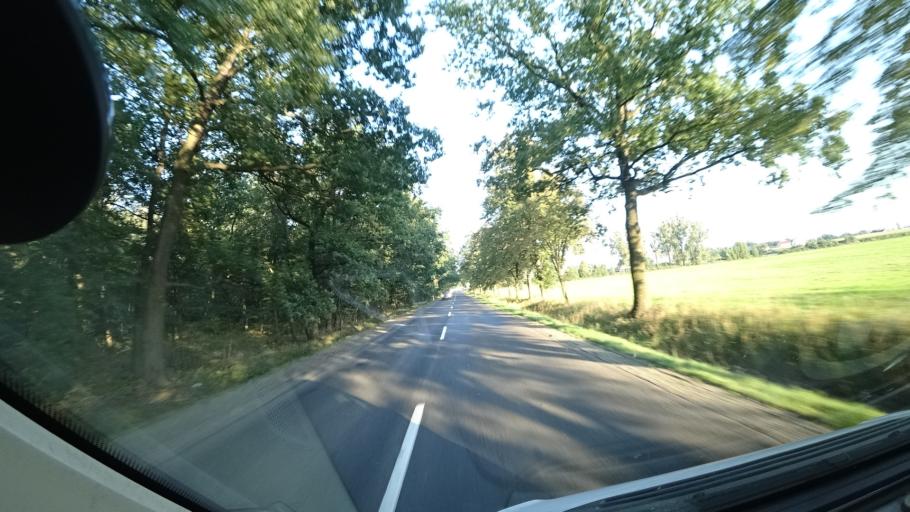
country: PL
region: Opole Voivodeship
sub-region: Powiat kedzierzynsko-kozielski
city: Bierawa
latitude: 50.2941
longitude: 18.2452
